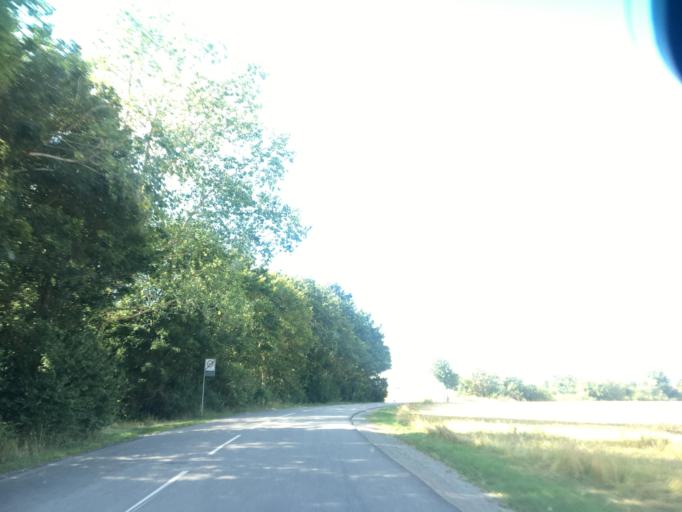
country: DK
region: Zealand
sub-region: Solrod Kommune
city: Solrod Strand
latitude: 55.5719
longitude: 12.2173
